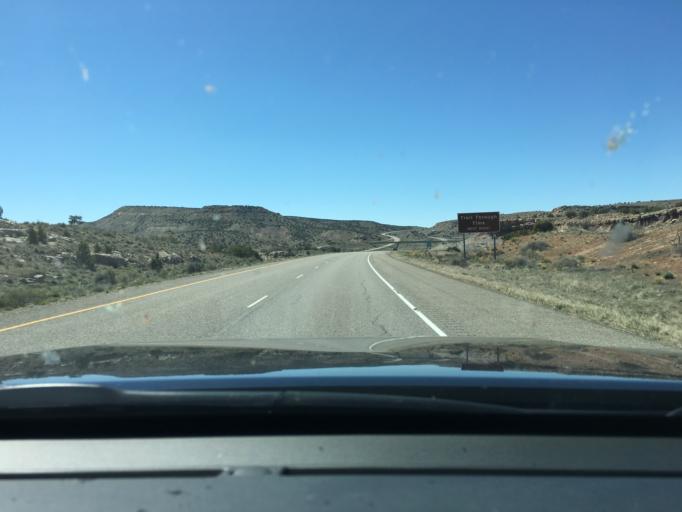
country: US
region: Colorado
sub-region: Mesa County
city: Loma
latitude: 39.1933
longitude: -109.0073
